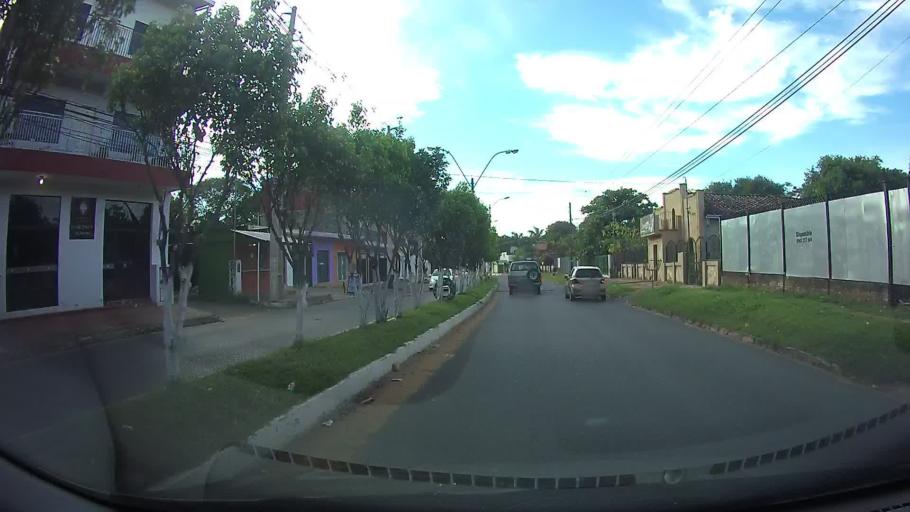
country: PY
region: Central
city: San Antonio
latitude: -25.4203
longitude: -57.5671
